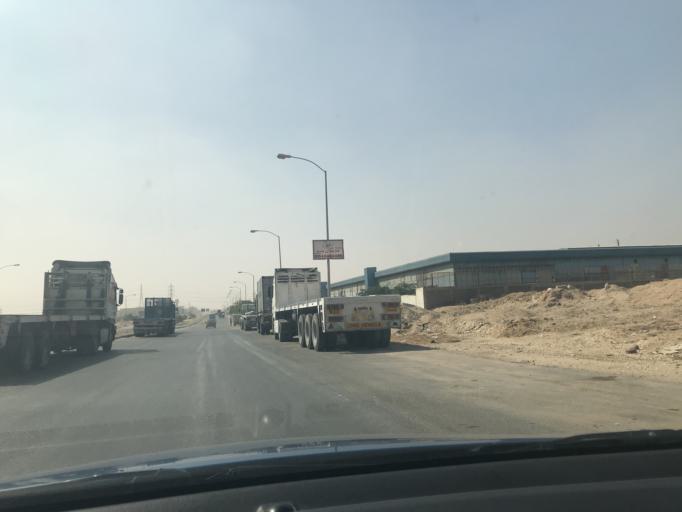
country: EG
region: Eastern Province
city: Bilbays
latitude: 30.2514
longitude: 31.7581
